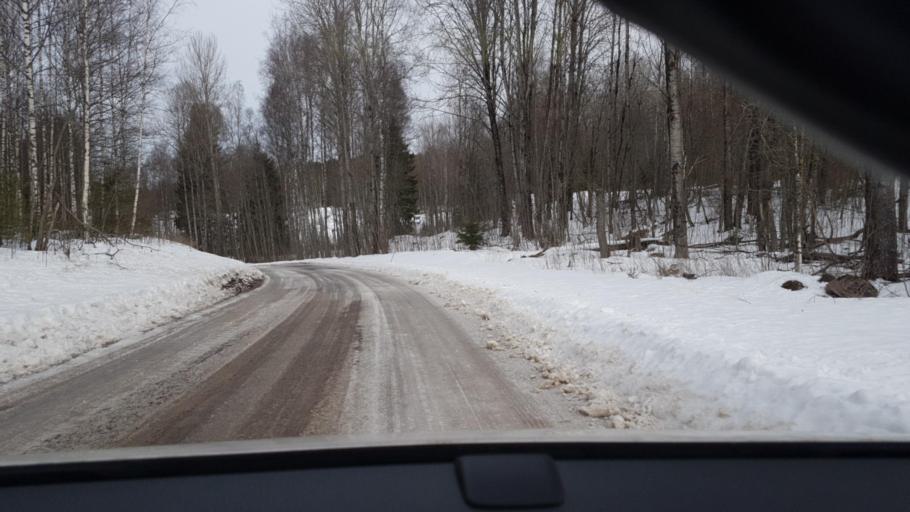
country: SE
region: Vaermland
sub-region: Eda Kommun
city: Amotfors
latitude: 59.8107
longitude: 12.3615
